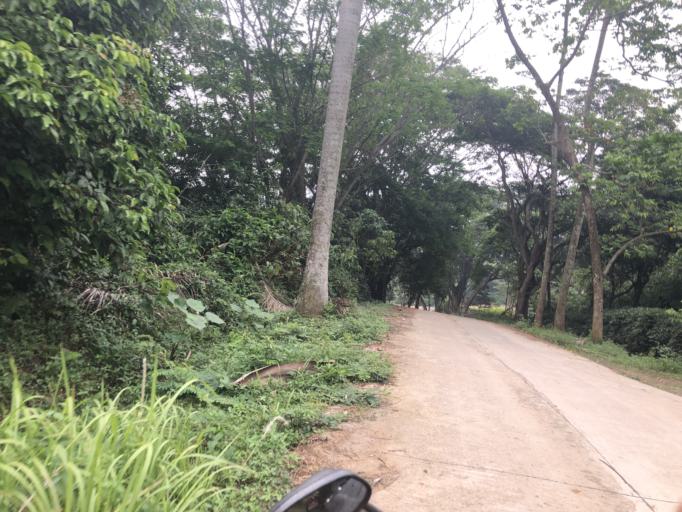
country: ID
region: West Java
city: Ciampea
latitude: -6.5474
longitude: 106.7155
